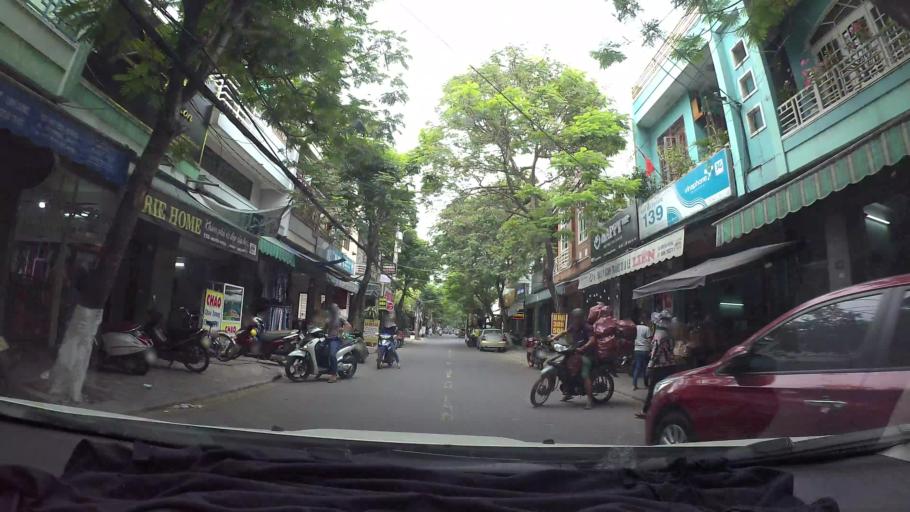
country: VN
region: Da Nang
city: Da Nang
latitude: 16.0616
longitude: 108.2138
